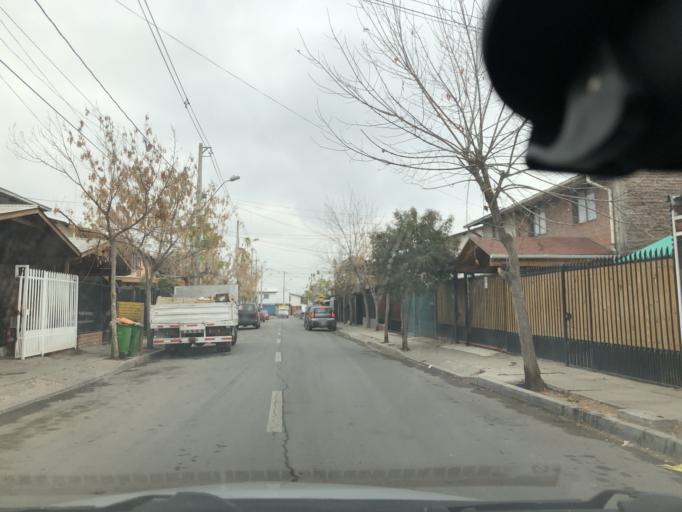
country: CL
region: Santiago Metropolitan
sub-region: Provincia de Santiago
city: La Pintana
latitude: -33.5729
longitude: -70.6078
